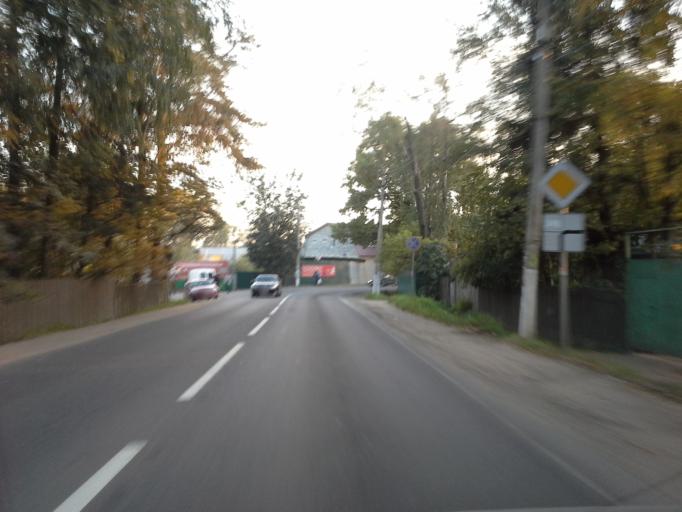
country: RU
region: Moskovskaya
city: Zhavoronki
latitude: 55.6439
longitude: 37.1008
